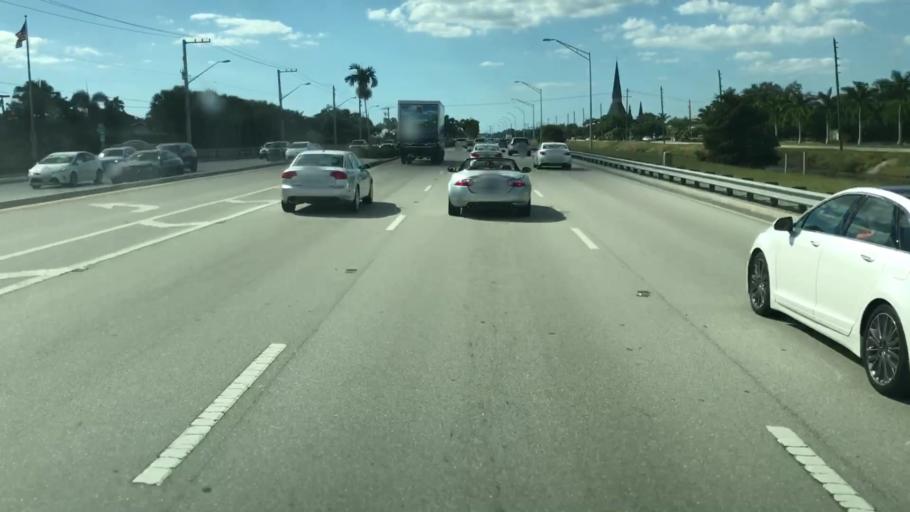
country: US
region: Florida
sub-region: Collier County
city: Naples Park
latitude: 26.2727
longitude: -81.7612
